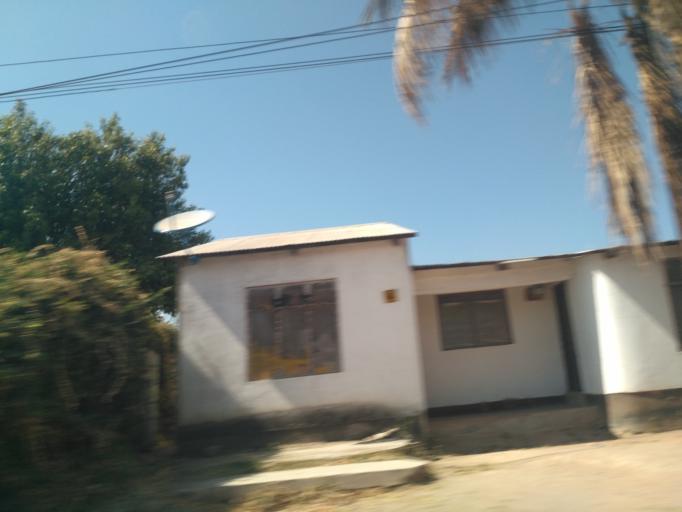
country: TZ
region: Dodoma
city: Dodoma
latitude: -6.1668
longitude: 35.7488
